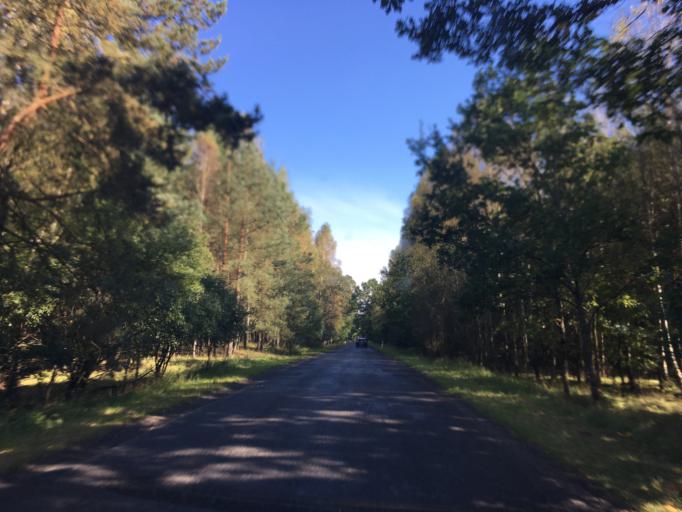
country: PL
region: Kujawsko-Pomorskie
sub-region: Powiat swiecki
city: Warlubie
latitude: 53.5978
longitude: 18.5776
